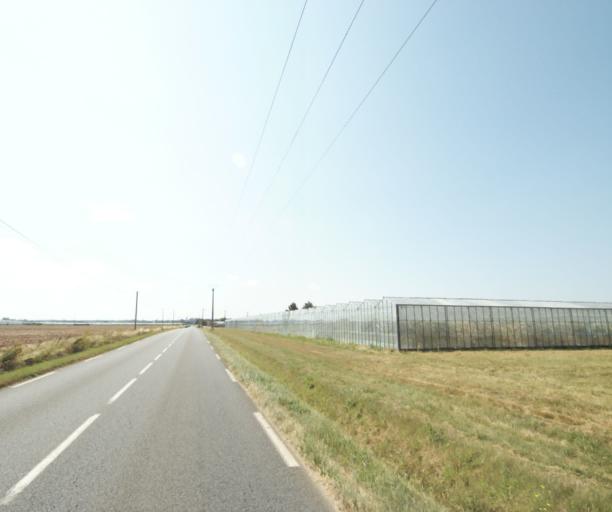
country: FR
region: Centre
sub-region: Departement du Loiret
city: Saint-Cyr-en-Val
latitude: 47.8510
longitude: 1.9545
